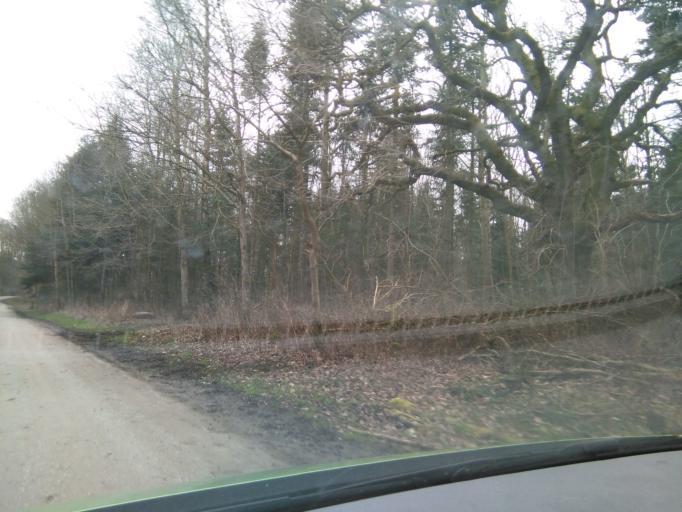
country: DK
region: Central Jutland
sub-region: Arhus Kommune
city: Beder
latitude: 56.0533
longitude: 10.2613
